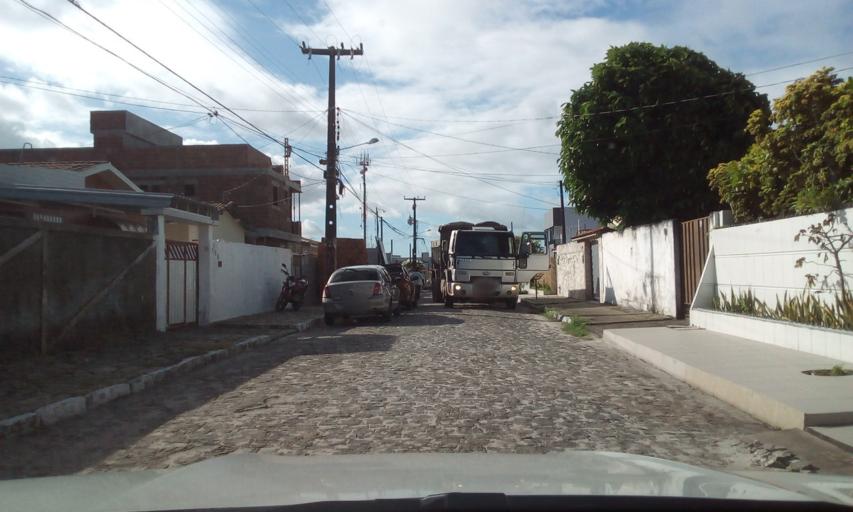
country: BR
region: Paraiba
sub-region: Joao Pessoa
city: Joao Pessoa
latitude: -7.1772
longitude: -34.8398
